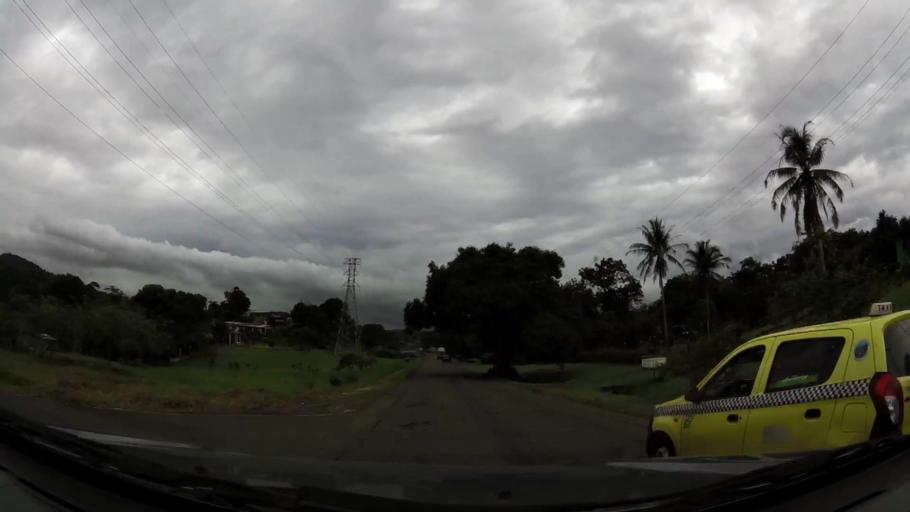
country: PA
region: Panama
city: Chilibre
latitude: 9.1394
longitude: -79.6150
